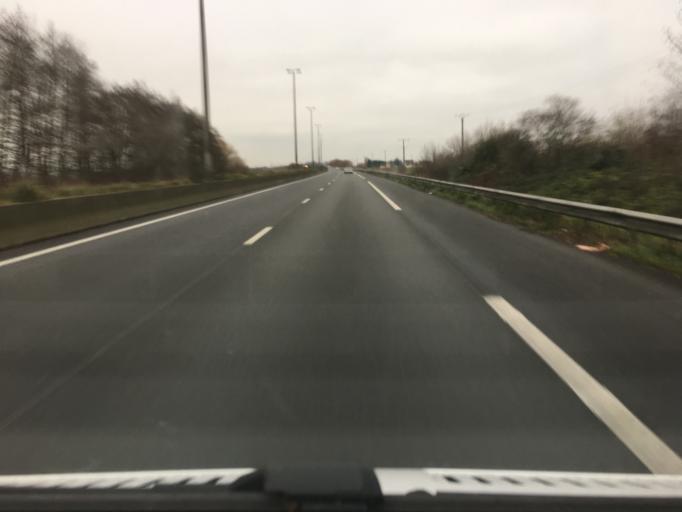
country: FR
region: Nord-Pas-de-Calais
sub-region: Departement du Pas-de-Calais
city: Oye-Plage
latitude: 50.9318
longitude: 2.0210
